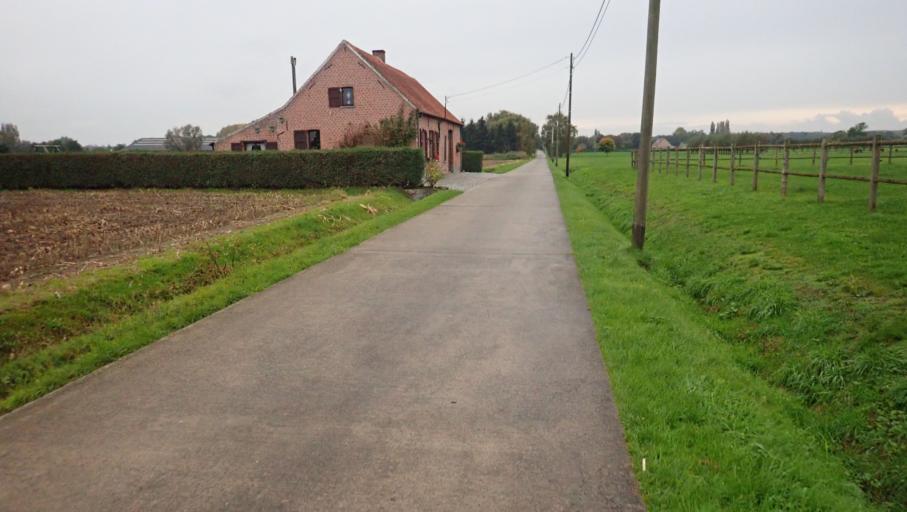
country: BE
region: Flanders
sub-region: Provincie Antwerpen
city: Berlaar
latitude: 51.1111
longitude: 4.6229
